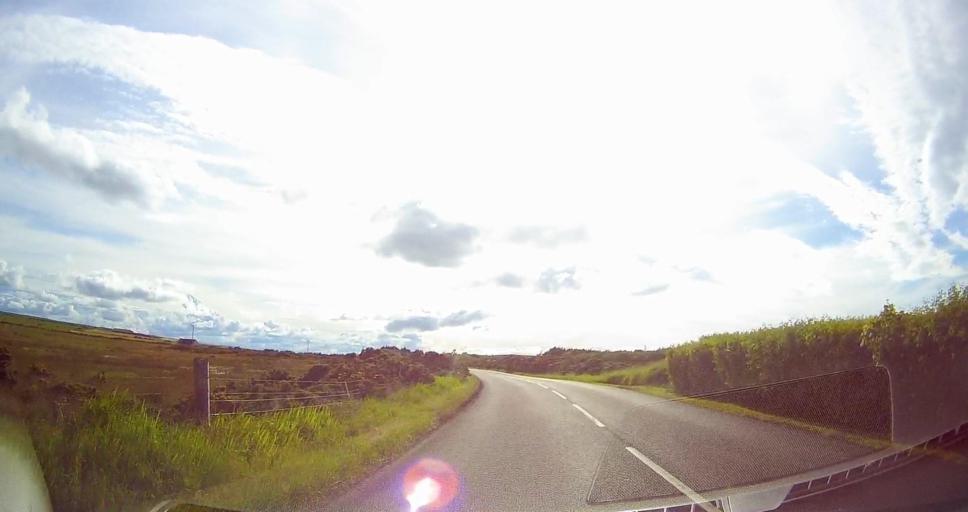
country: GB
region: Scotland
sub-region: Highland
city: Thurso
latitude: 58.6293
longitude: -3.3117
